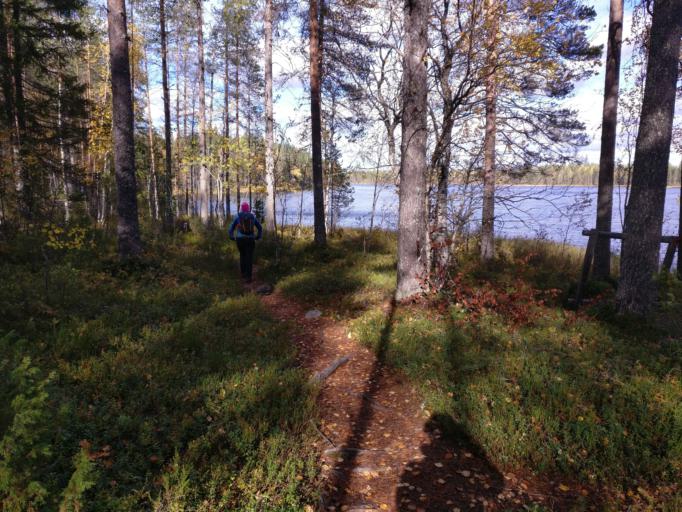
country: FI
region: Northern Savo
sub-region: Koillis-Savo
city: Rautavaara
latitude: 63.6241
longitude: 28.3234
